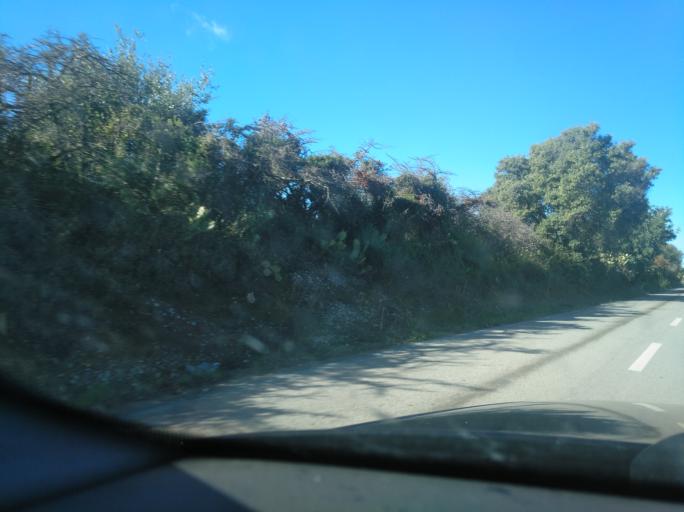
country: PT
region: Faro
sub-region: Vila Real de Santo Antonio
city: Monte Gordo
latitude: 37.1679
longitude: -7.5362
